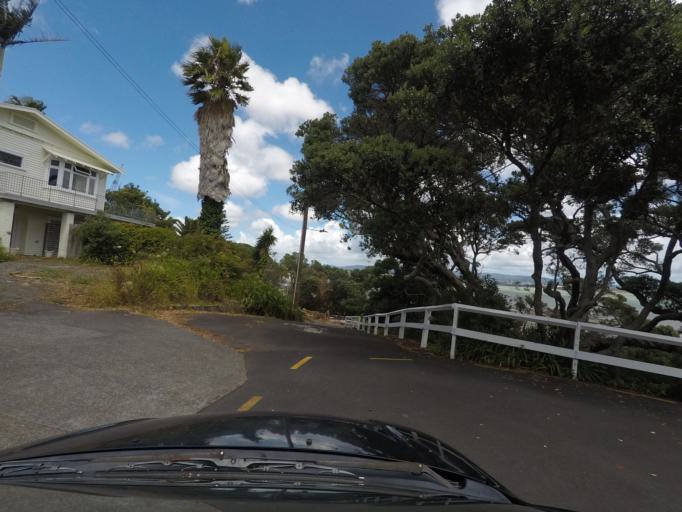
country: NZ
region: Auckland
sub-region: Auckland
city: Rosebank
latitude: -36.8619
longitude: 174.6996
